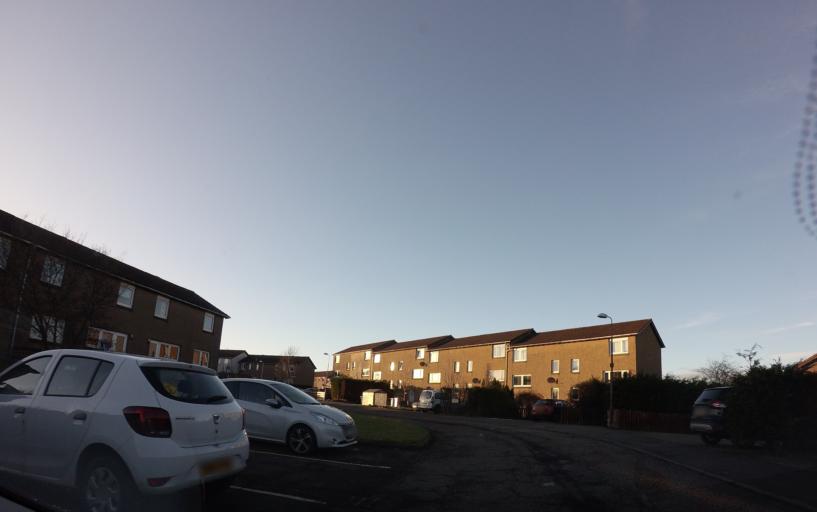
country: GB
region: Scotland
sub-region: West Lothian
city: Livingston
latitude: 55.9038
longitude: -3.5402
